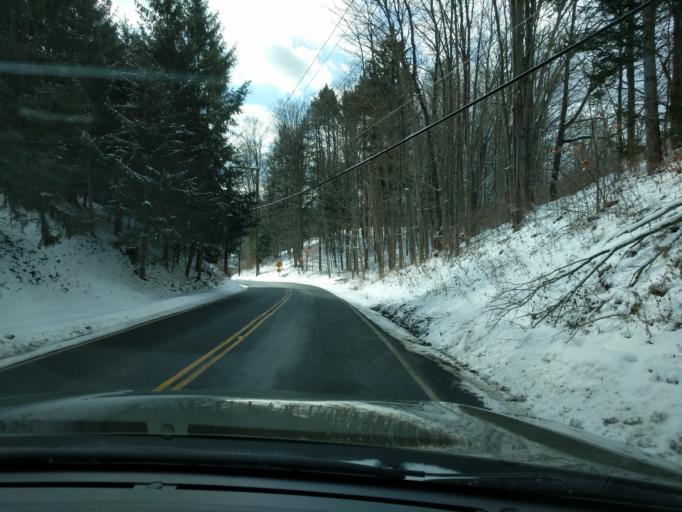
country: US
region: New York
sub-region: Tompkins County
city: East Ithaca
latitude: 42.3836
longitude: -76.3869
